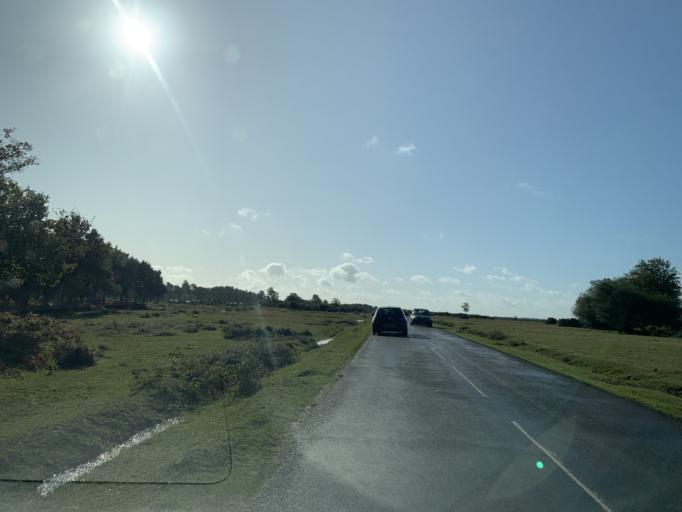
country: GB
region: England
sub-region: Hampshire
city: Cadnam
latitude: 50.9240
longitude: -1.6533
